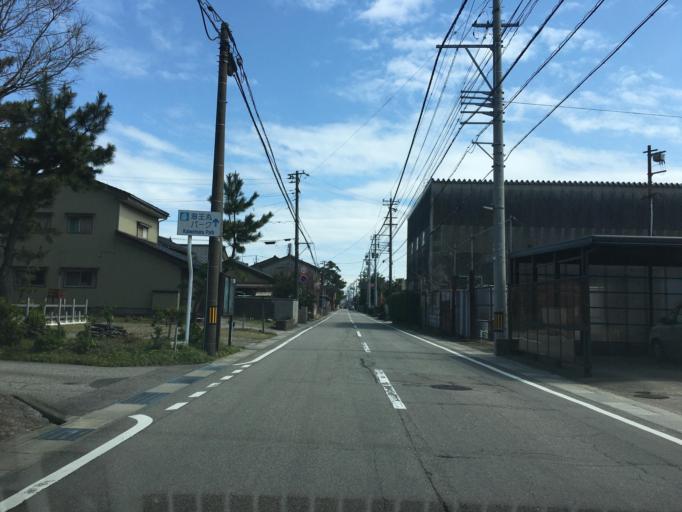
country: JP
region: Toyama
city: Nishishinminato
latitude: 36.7780
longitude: 137.1006
